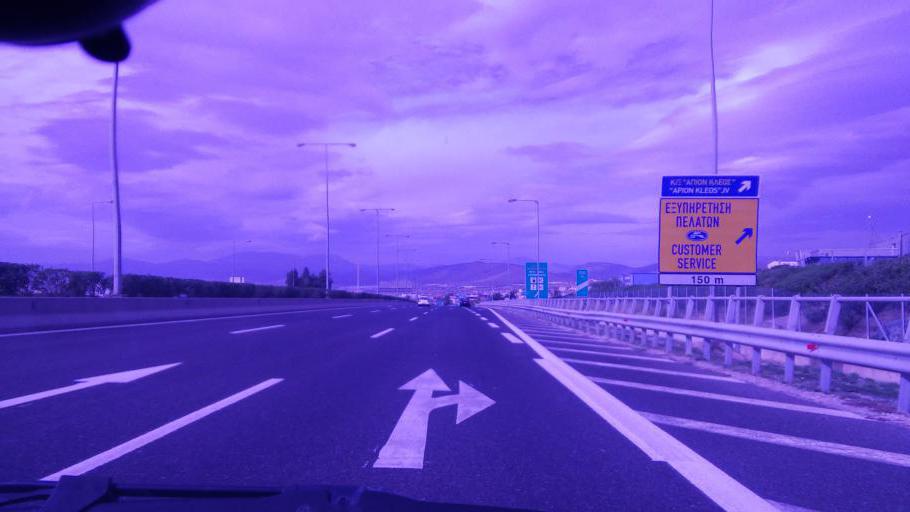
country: GR
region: Attica
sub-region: Nomarchia Dytikis Attikis
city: Aspropyrgos
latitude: 38.0922
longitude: 23.6105
